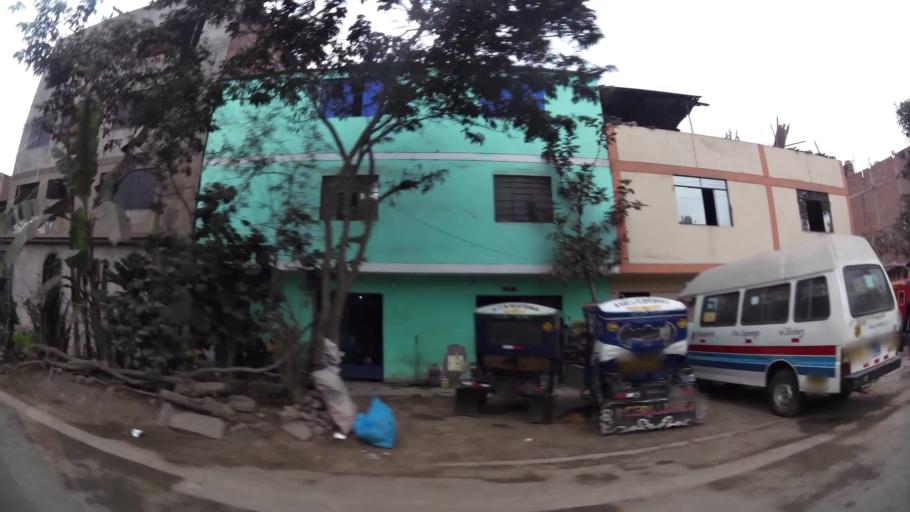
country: PE
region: Lima
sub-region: Lima
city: Vitarte
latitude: -12.0362
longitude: -76.9662
